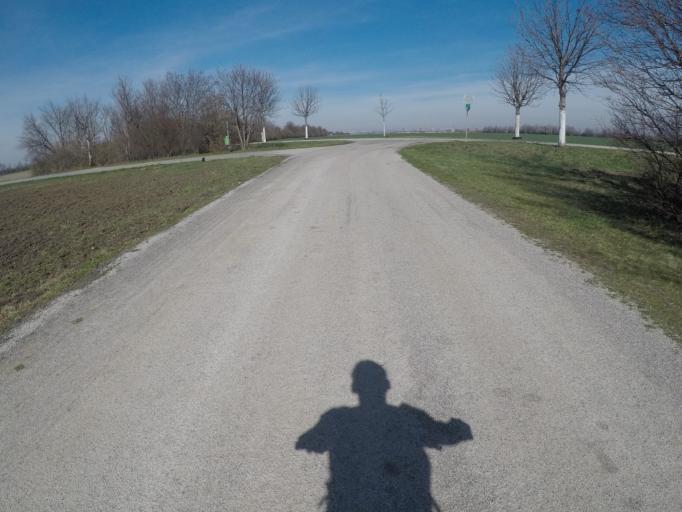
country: AT
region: Lower Austria
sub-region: Politischer Bezirk Modling
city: Biedermannsdorf
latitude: 48.1012
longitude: 16.3415
